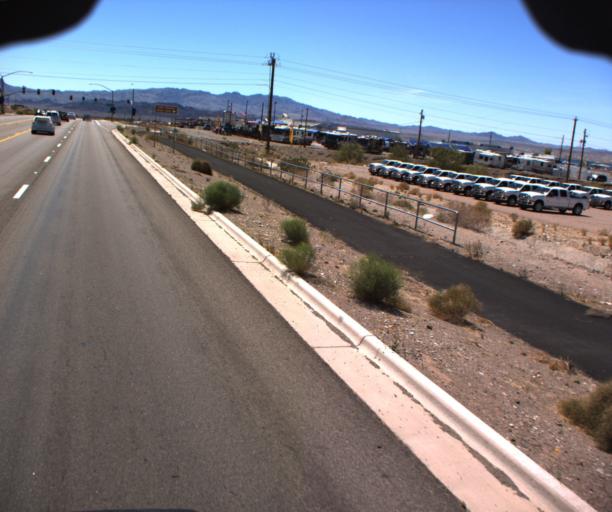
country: US
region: Arizona
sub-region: Mohave County
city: Lake Havasu City
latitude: 34.4952
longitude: -114.3495
